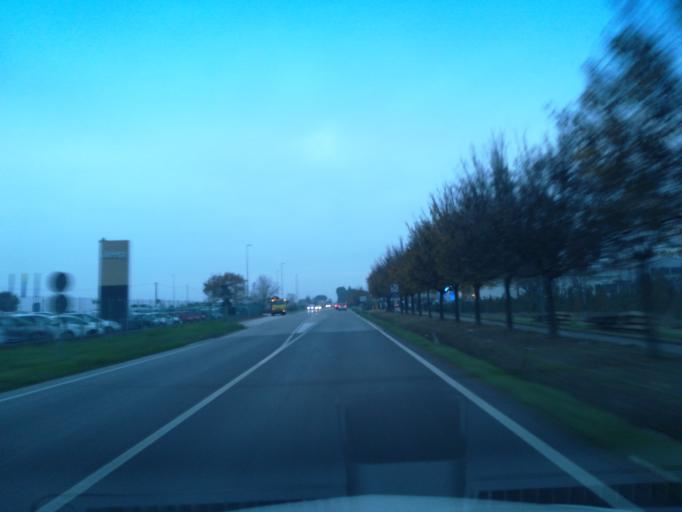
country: IT
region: Emilia-Romagna
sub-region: Provincia di Ravenna
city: Faenza
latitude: 44.2993
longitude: 11.8500
